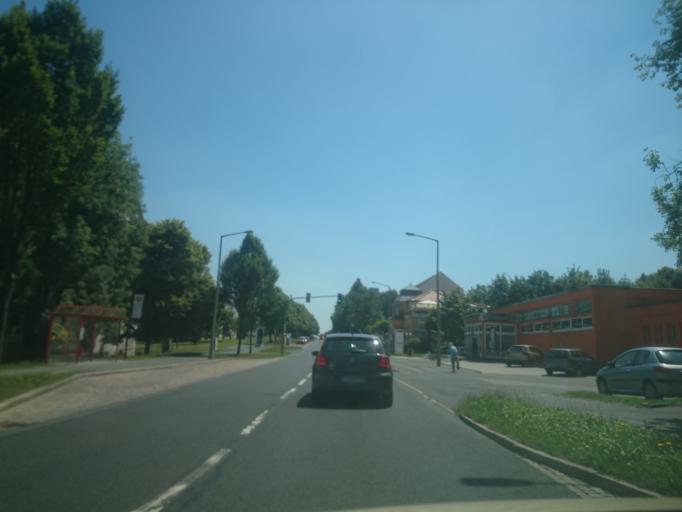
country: DE
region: Saxony
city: Freiberg
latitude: 50.9056
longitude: 13.3221
